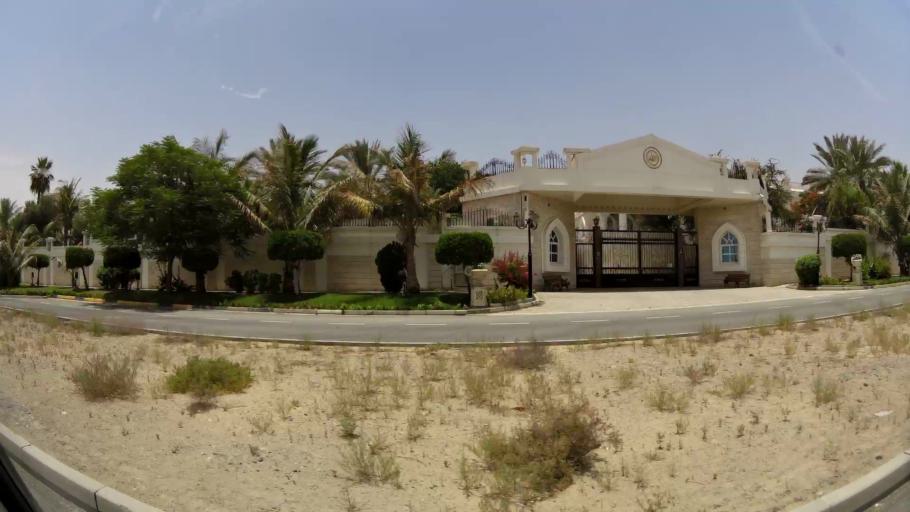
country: AE
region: Ash Shariqah
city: Sharjah
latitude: 25.2382
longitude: 55.4522
